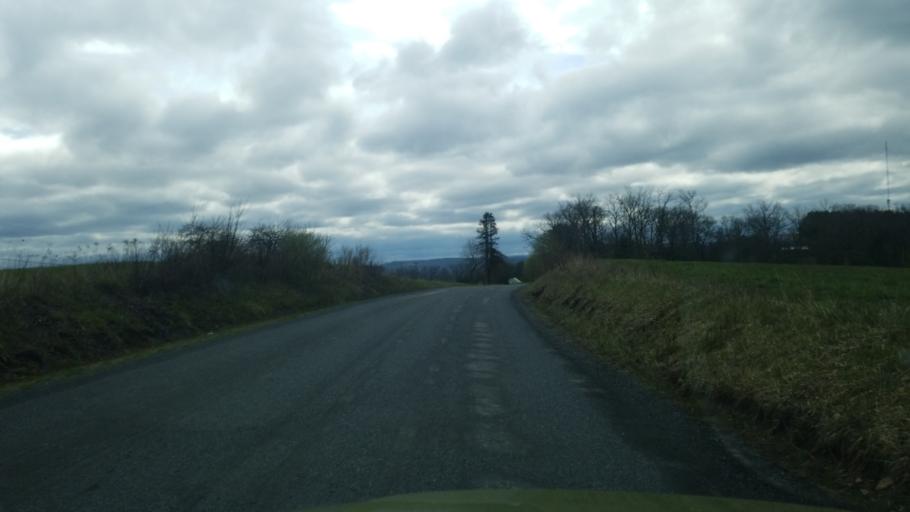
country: US
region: Pennsylvania
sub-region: Clearfield County
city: Clearfield
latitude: 41.0774
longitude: -78.3748
